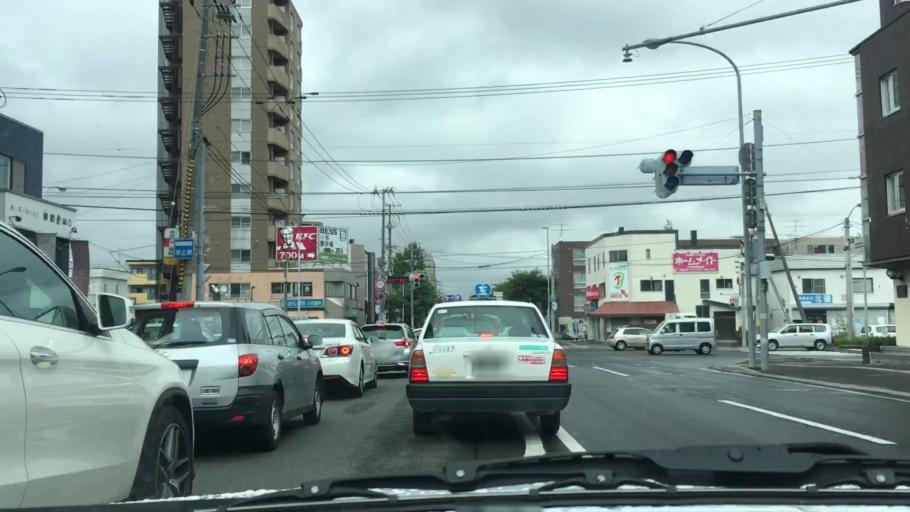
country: JP
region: Hokkaido
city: Sapporo
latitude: 43.0800
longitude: 141.3641
